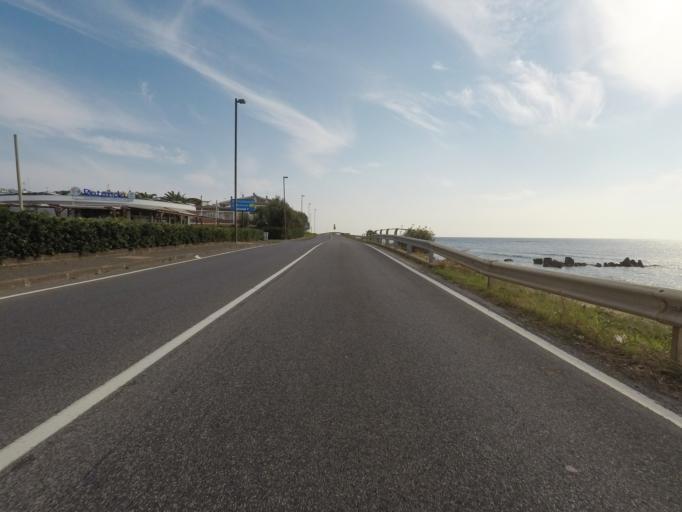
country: IT
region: Latium
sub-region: Citta metropolitana di Roma Capitale
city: Santa Marinella
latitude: 42.0435
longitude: 11.8273
